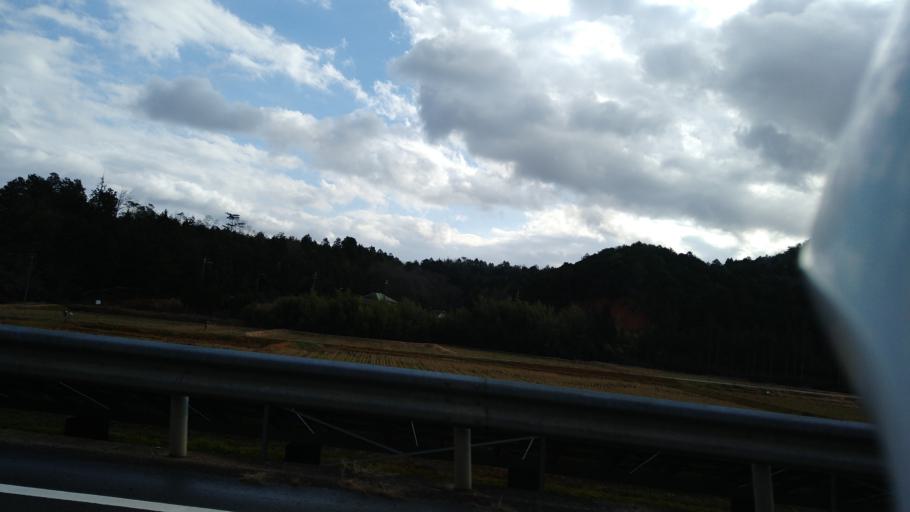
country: JP
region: Kyoto
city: Ayabe
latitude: 35.1738
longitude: 135.3613
